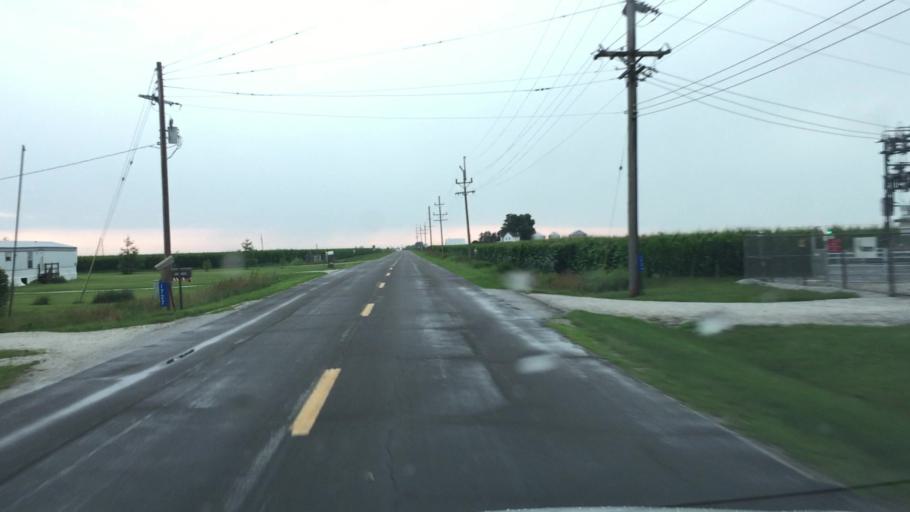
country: US
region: Illinois
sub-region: Hancock County
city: Carthage
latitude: 40.5207
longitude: -91.1707
